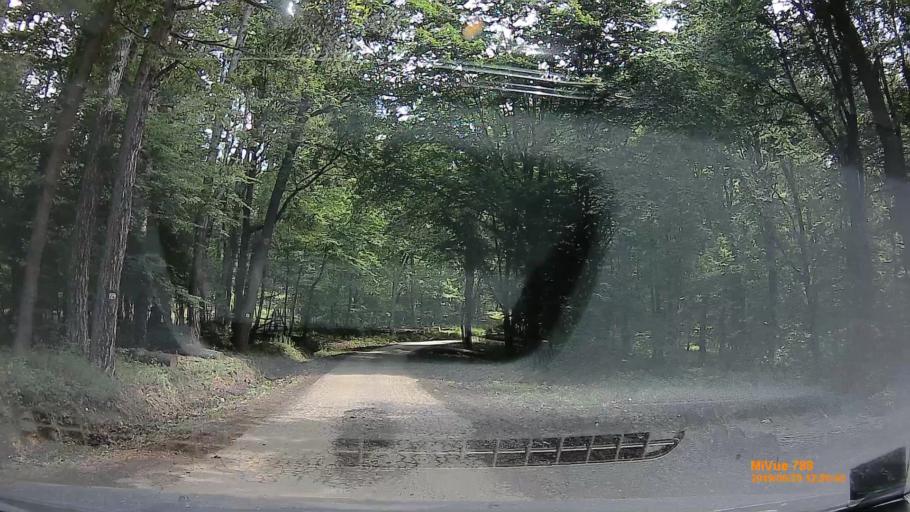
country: HU
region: Baranya
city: Hosszuheteny
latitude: 46.2146
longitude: 18.3510
